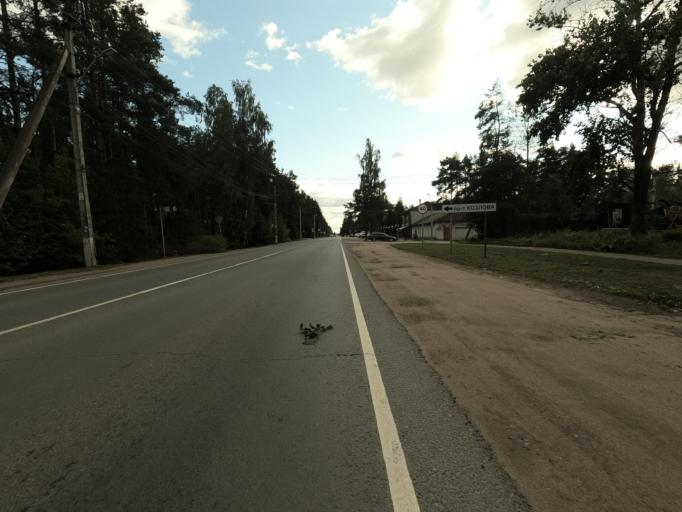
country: RU
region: Leningrad
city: Vsevolozhsk
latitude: 59.9993
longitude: 30.6613
